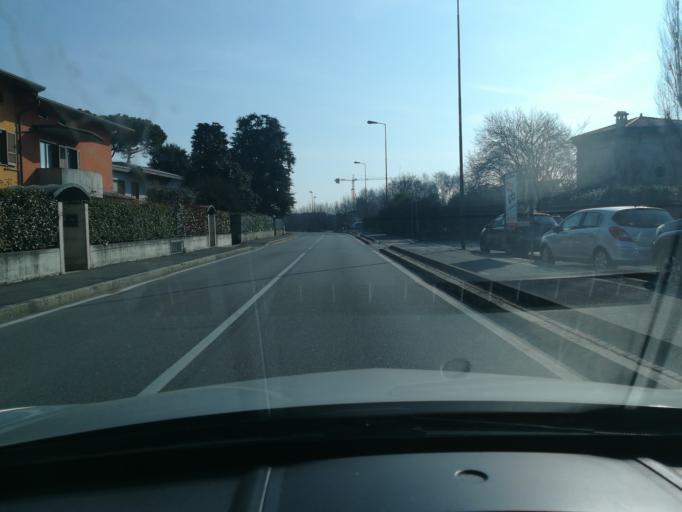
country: IT
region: Lombardy
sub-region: Provincia di Bergamo
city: Stezzano
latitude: 45.6524
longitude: 9.6551
